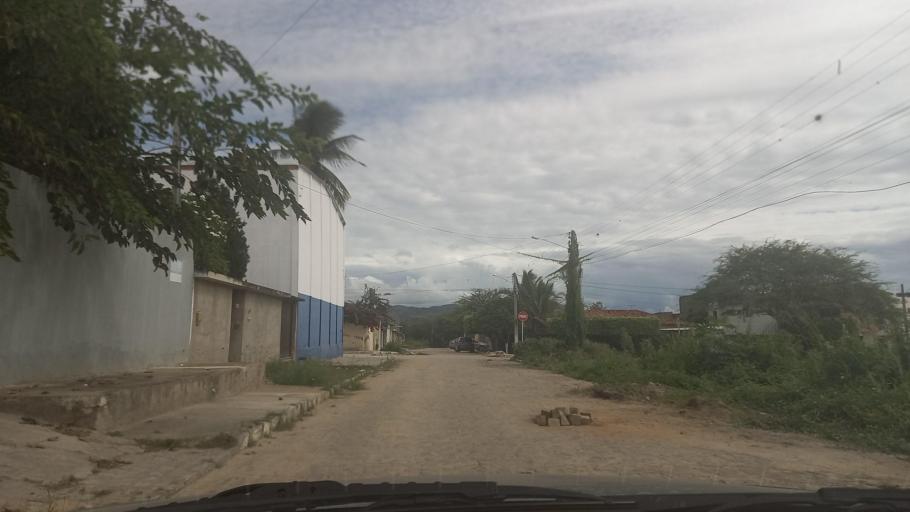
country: BR
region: Pernambuco
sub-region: Caruaru
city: Caruaru
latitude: -8.2922
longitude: -35.9910
